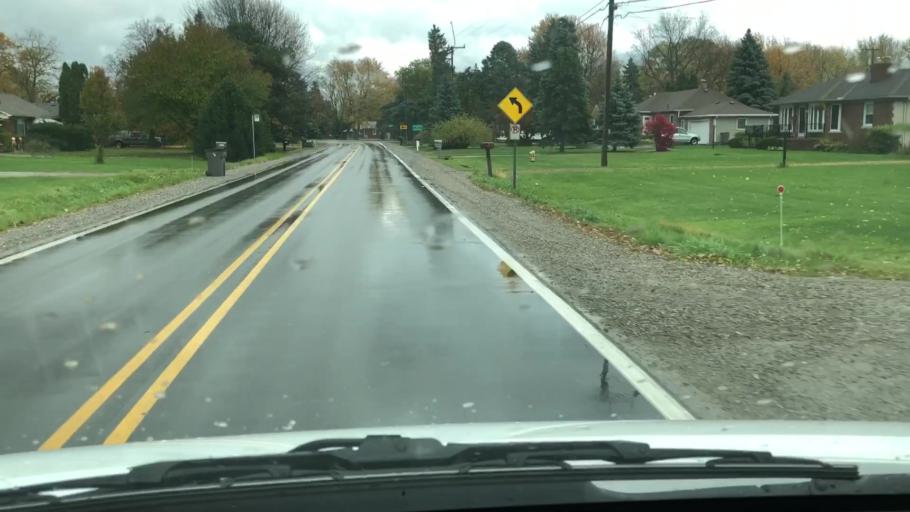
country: US
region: Michigan
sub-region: Macomb County
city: Fraser
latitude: 42.5664
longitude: -82.9434
